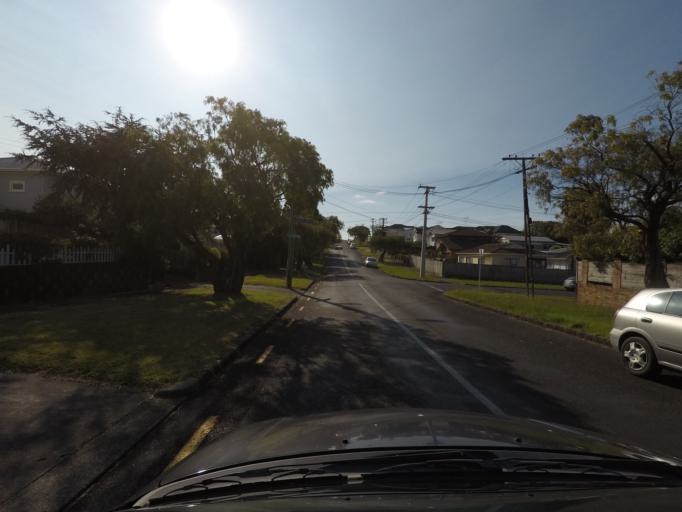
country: NZ
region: Auckland
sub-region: Auckland
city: Auckland
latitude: -36.9007
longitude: 174.7408
